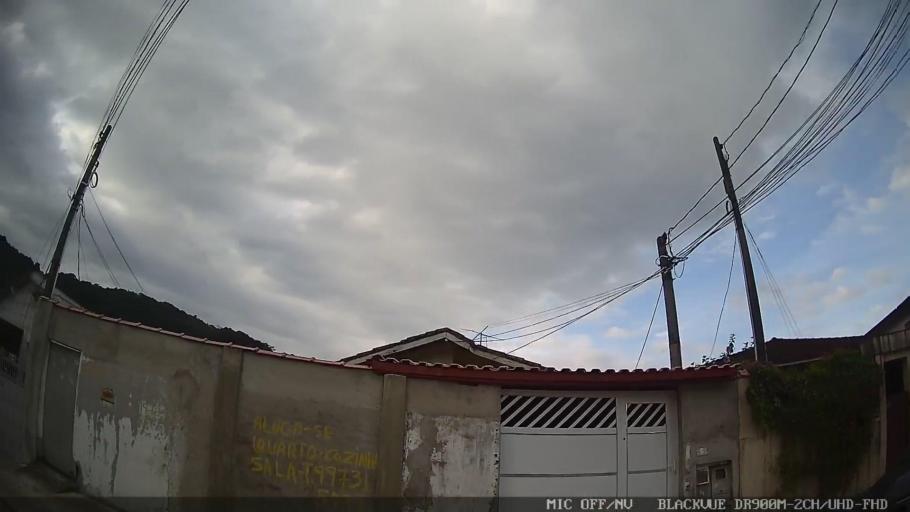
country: BR
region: Sao Paulo
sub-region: Guaruja
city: Guaruja
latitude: -23.9825
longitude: -46.2450
